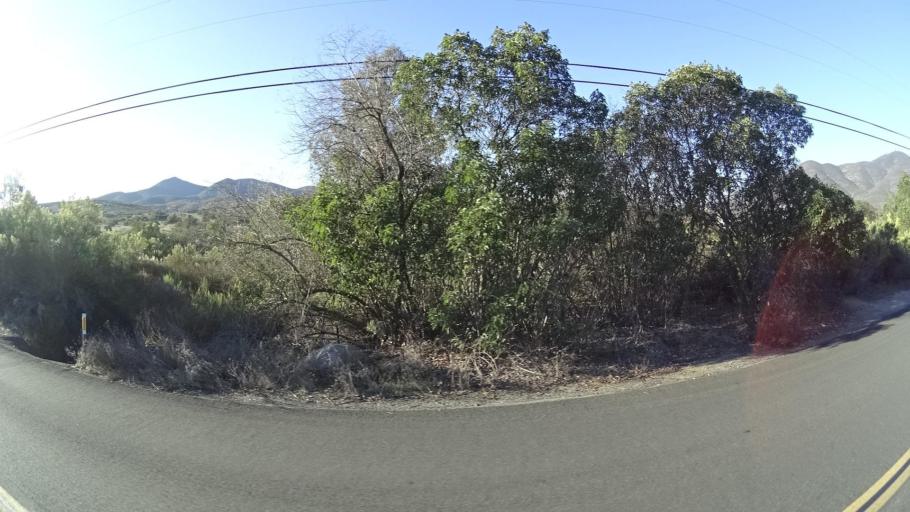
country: US
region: California
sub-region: San Diego County
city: Jamul
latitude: 32.7041
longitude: -116.8944
